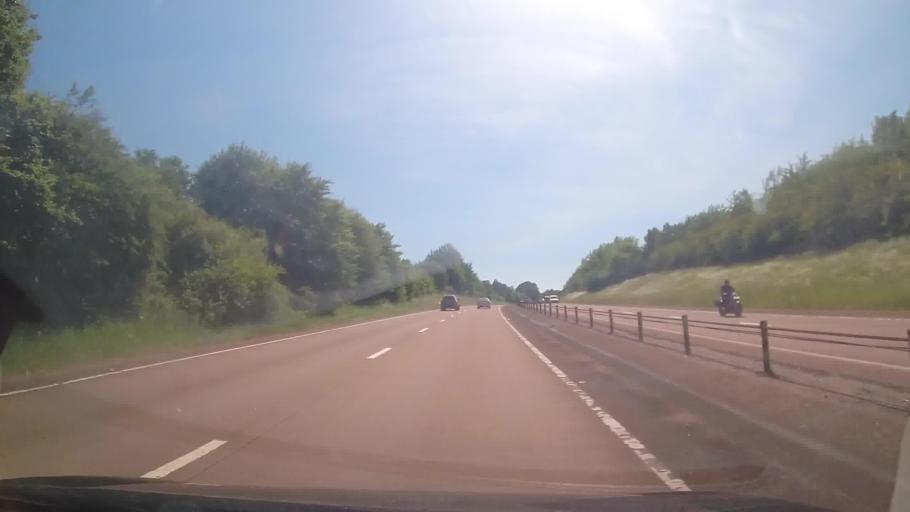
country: GB
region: England
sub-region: Devon
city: Newton Poppleford
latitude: 50.7379
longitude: -3.3666
